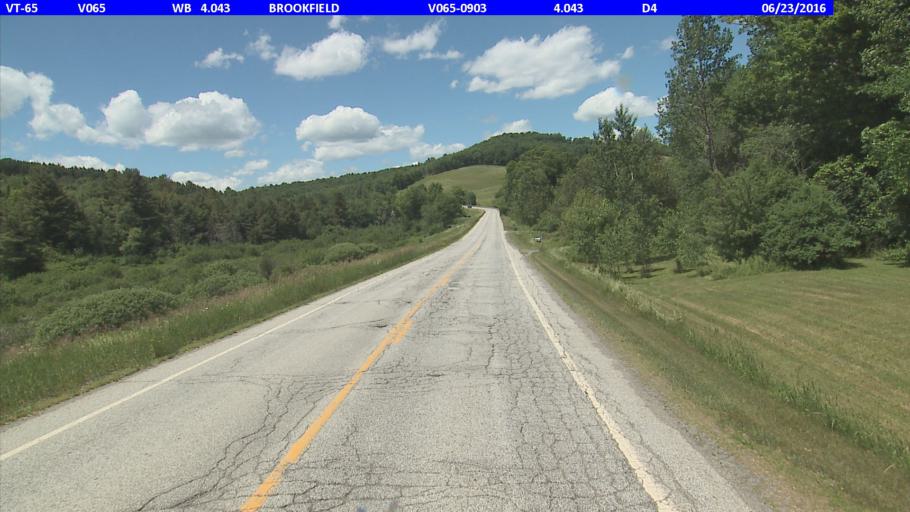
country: US
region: Vermont
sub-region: Orange County
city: Williamstown
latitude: 44.0323
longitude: -72.5907
